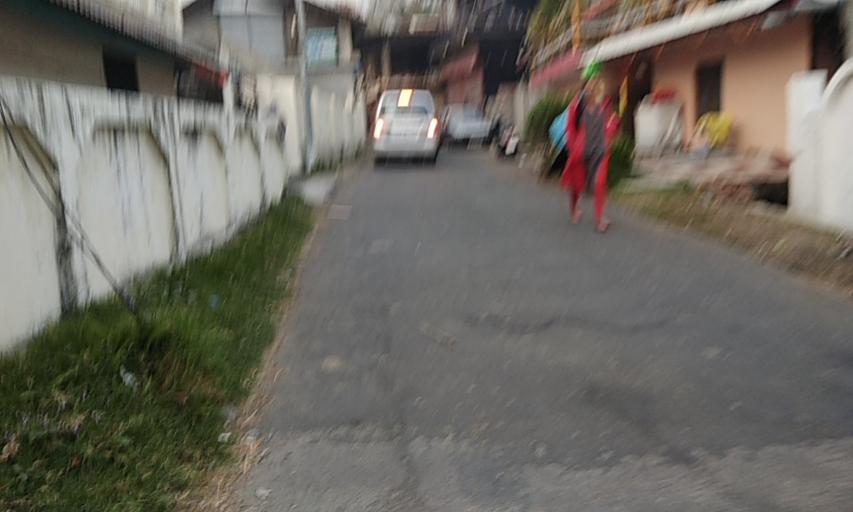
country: IN
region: Himachal Pradesh
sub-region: Kangra
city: Palampur
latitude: 32.1191
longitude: 76.5333
